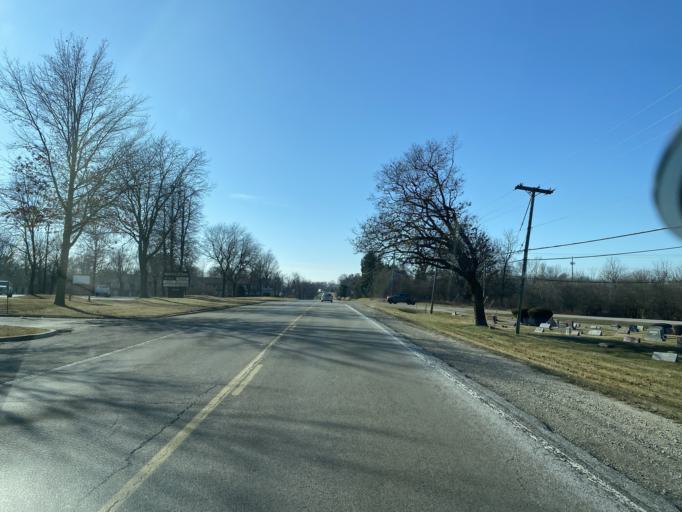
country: US
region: Illinois
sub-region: Will County
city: Lockport
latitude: 41.6089
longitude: -88.0448
